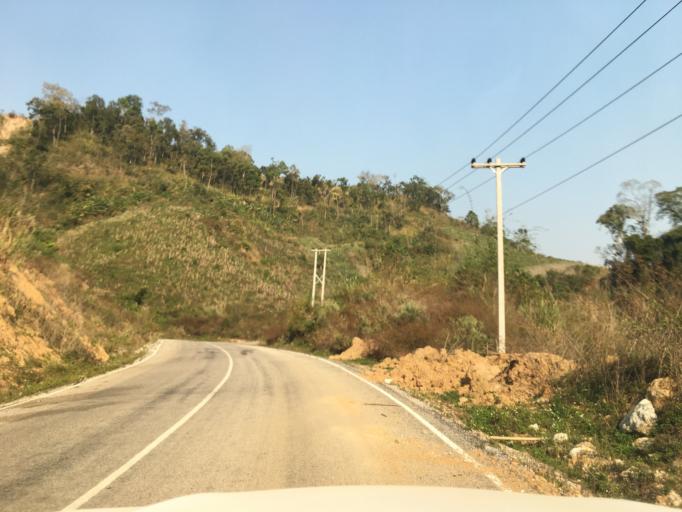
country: LA
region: Houaphan
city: Xam Nua
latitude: 20.5683
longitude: 104.0556
